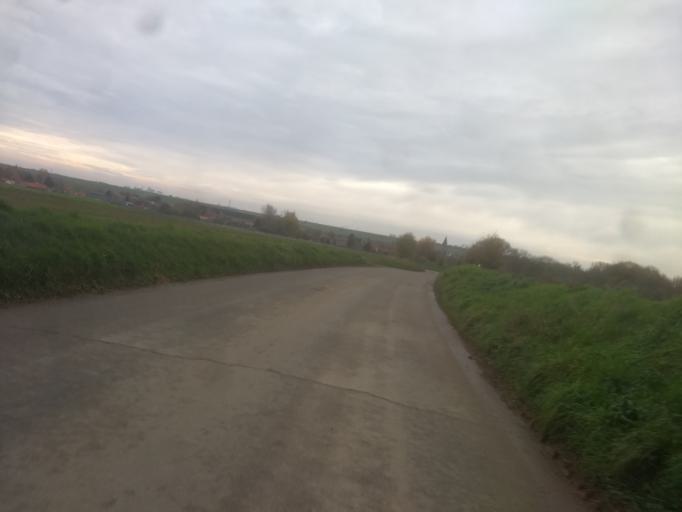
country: FR
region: Nord-Pas-de-Calais
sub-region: Departement du Pas-de-Calais
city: Dainville
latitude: 50.2529
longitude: 2.7219
